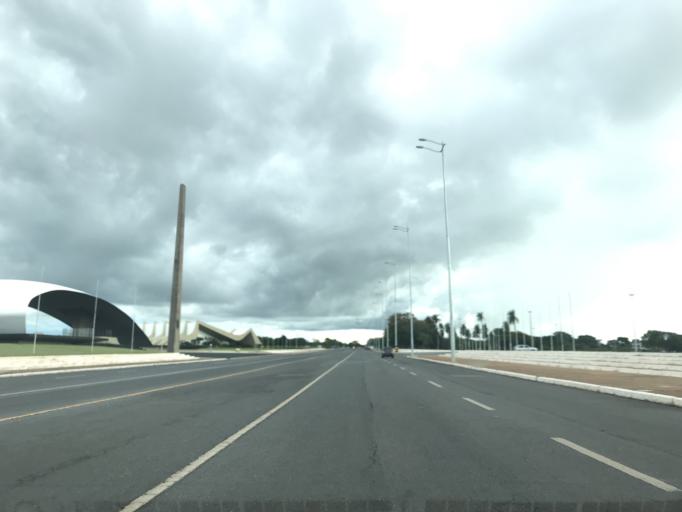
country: BR
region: Federal District
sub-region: Brasilia
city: Brasilia
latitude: -15.7719
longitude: -47.9197
